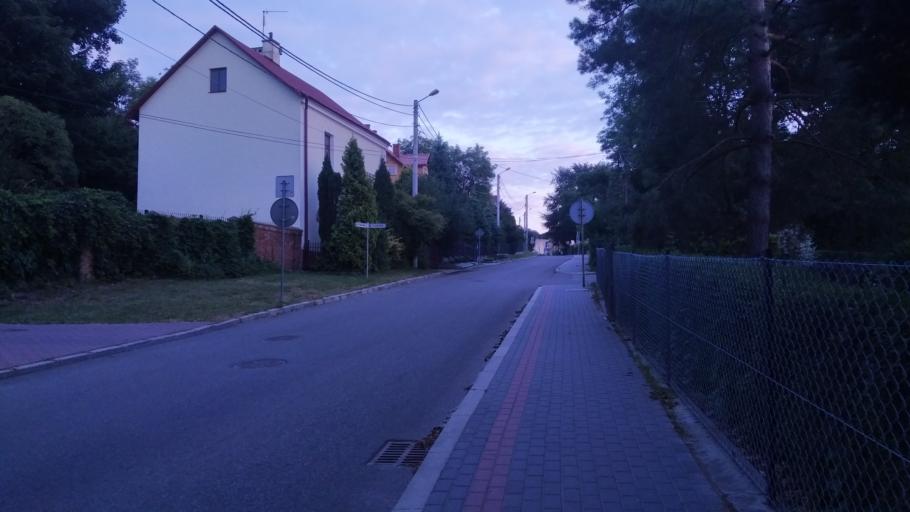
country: PL
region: Subcarpathian Voivodeship
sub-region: Powiat lancucki
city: Lancut
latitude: 50.0727
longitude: 22.2308
